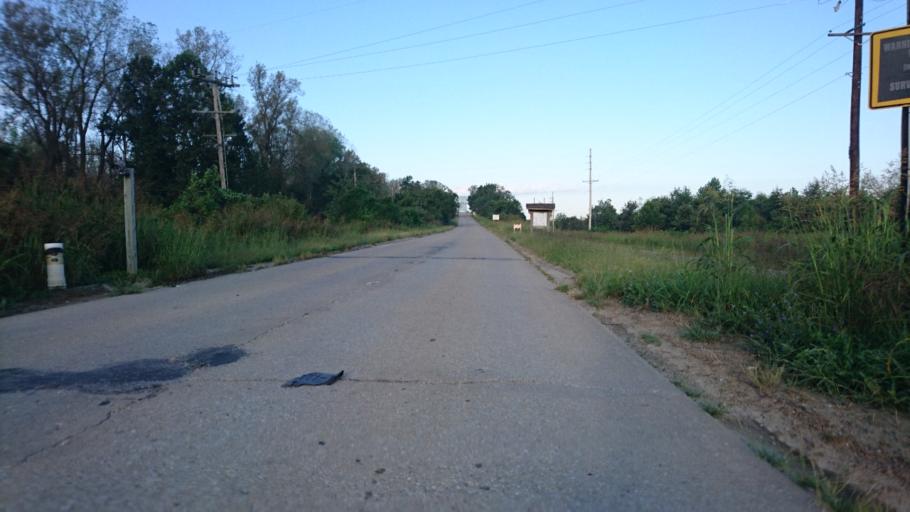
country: US
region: Illinois
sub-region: Madison County
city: Mitchell
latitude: 38.7621
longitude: -90.1303
